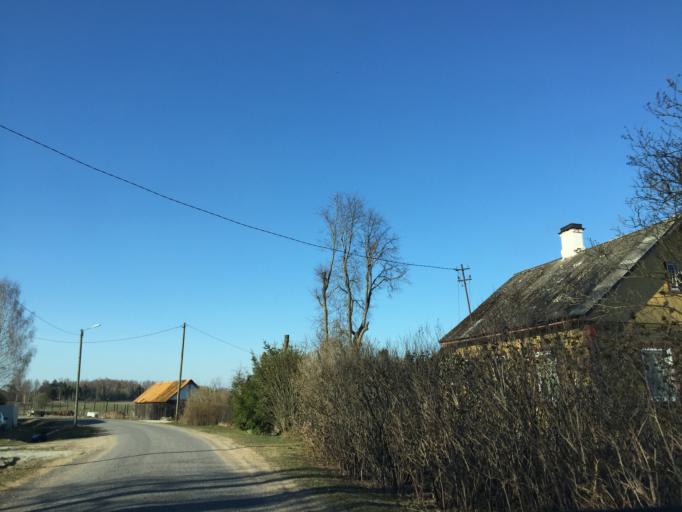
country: EE
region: Ida-Virumaa
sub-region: Sillamaee linn
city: Sillamae
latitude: 59.1247
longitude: 27.8034
